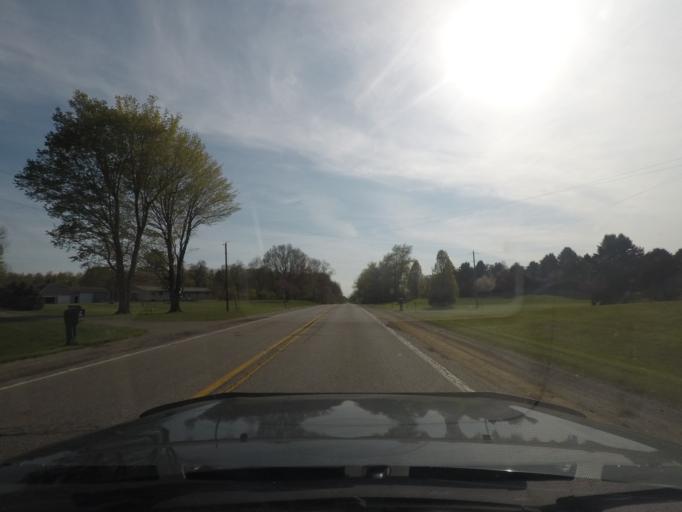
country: US
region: Michigan
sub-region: Berrien County
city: Buchanan
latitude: 41.8029
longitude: -86.4029
